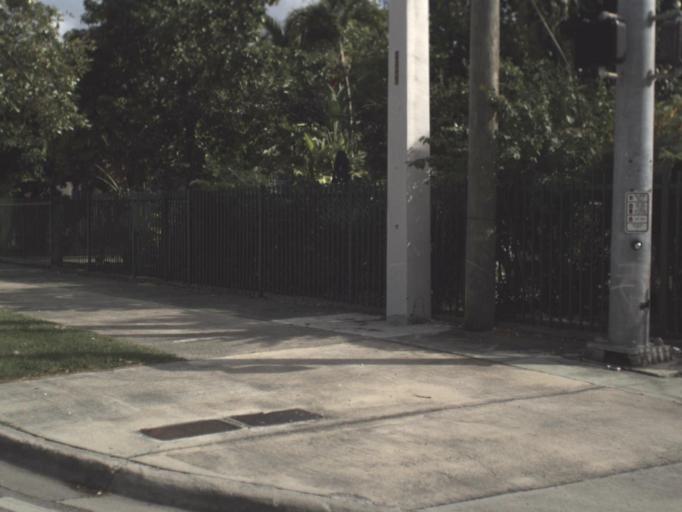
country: US
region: Florida
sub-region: Miami-Dade County
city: Leisure City
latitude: 25.4995
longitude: -80.4246
